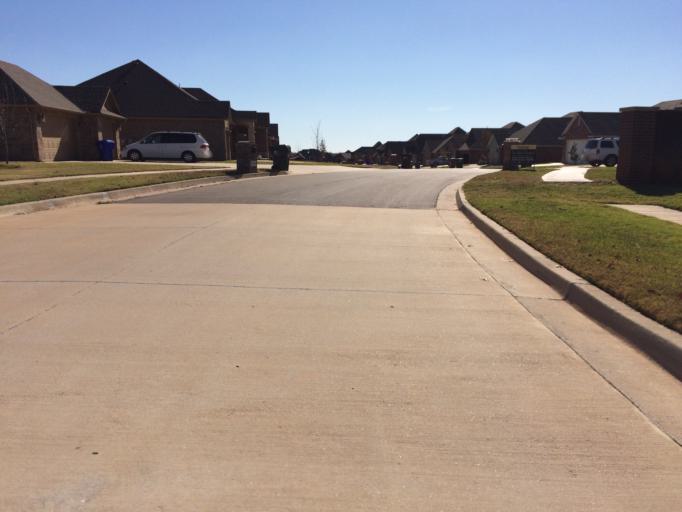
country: US
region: Oklahoma
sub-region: Cleveland County
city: Noble
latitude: 35.1716
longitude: -97.4229
